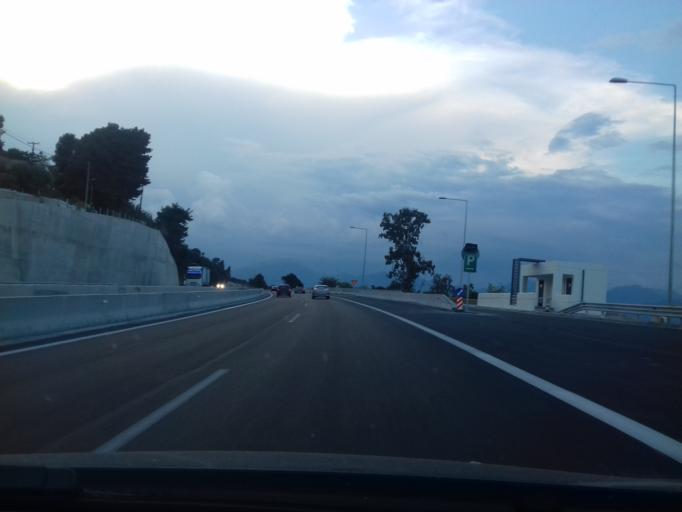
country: GR
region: West Greece
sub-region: Nomos Achaias
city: Kamarai
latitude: 38.3101
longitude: 21.9872
